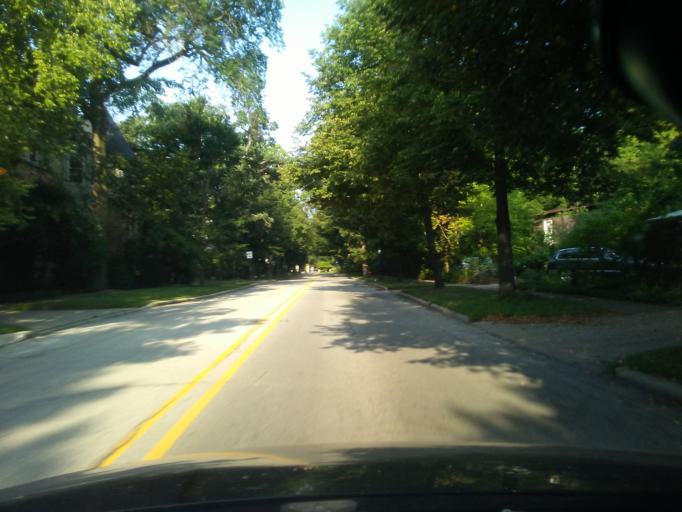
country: US
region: Illinois
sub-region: Cook County
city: Evanston
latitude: 42.0404
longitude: -87.6727
